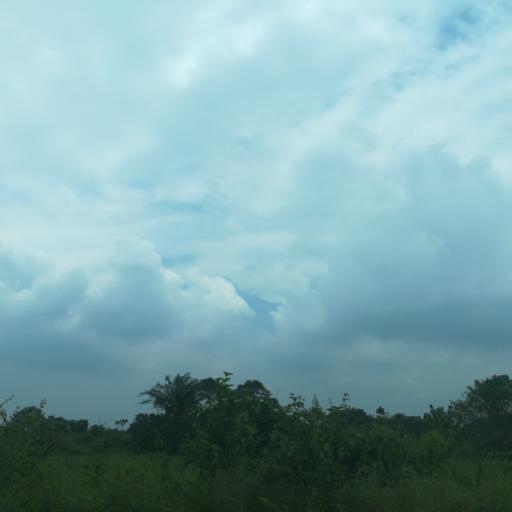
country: NG
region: Lagos
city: Ejirin
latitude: 6.6691
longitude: 3.7949
